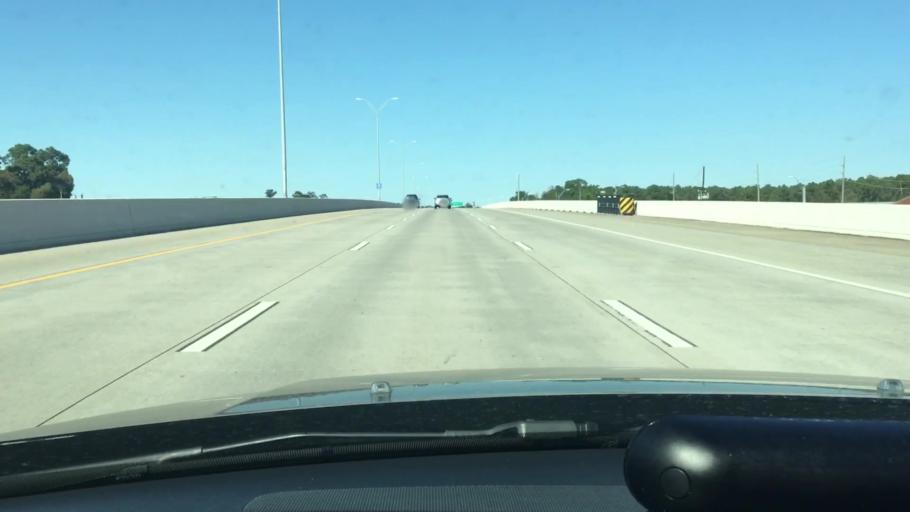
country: US
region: Texas
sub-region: Harris County
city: Sheldon
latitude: 29.8820
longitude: -95.1968
